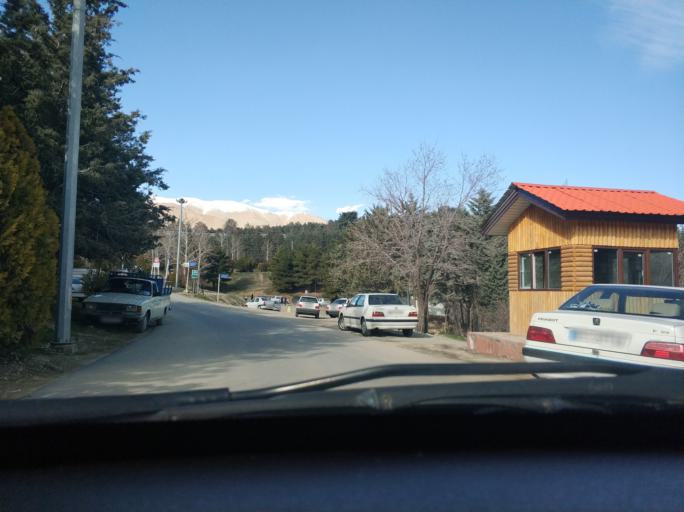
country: IR
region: Tehran
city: Tajrish
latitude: 35.8038
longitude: 51.5687
